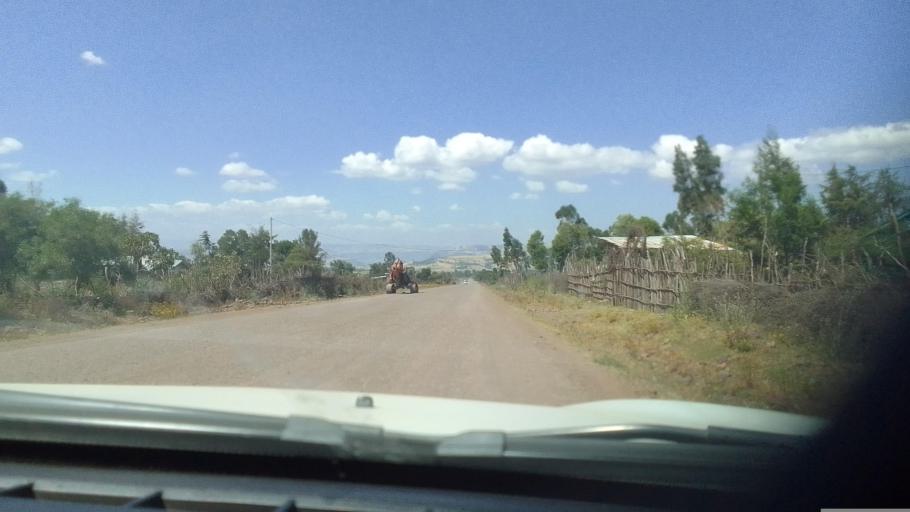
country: ET
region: Oromiya
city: Hagere Hiywet
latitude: 8.9246
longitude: 37.8630
